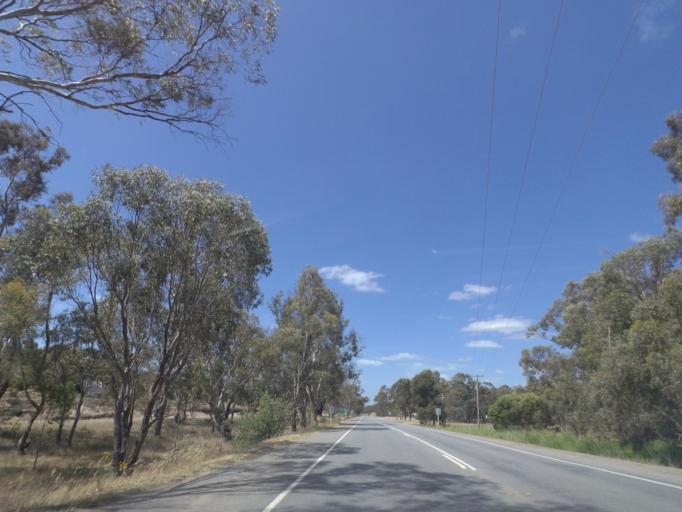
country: AU
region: Victoria
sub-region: Wangaratta
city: Wangaratta
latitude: -36.4629
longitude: 146.2275
